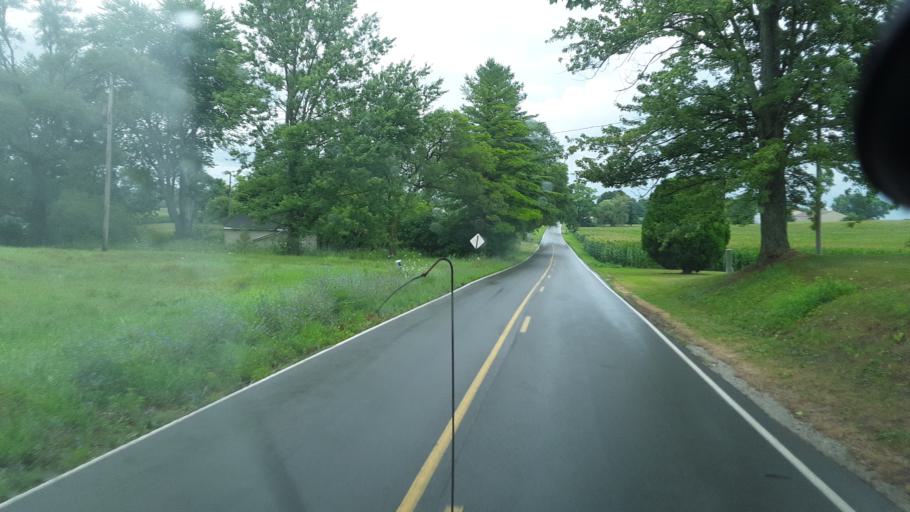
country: US
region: Indiana
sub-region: Steuben County
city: Hamilton
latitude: 41.6157
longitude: -84.8363
